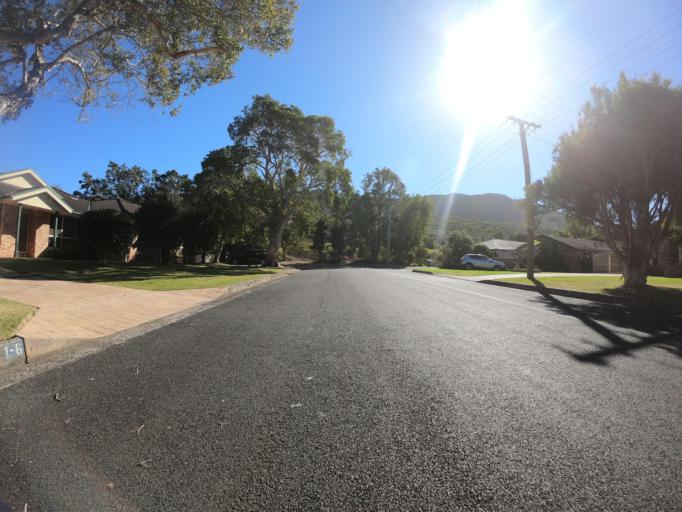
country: AU
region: New South Wales
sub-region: Wollongong
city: Bulli
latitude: -34.3128
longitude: 150.9238
